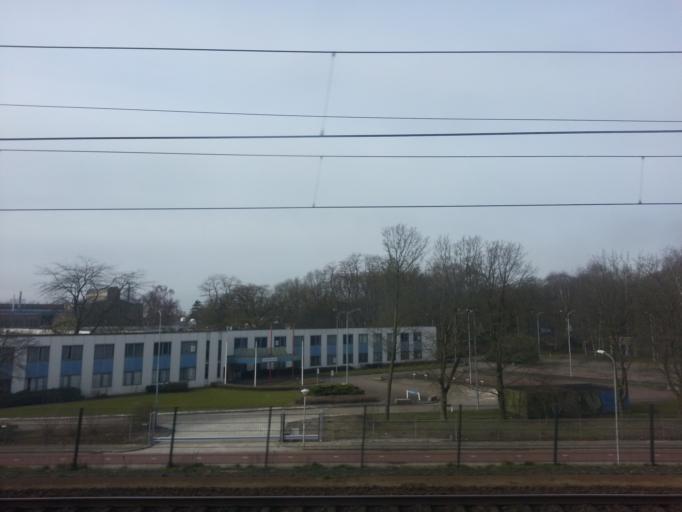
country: NL
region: North Brabant
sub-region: Gemeente Eindhoven
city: Eindhoven
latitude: 51.4554
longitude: 5.4502
